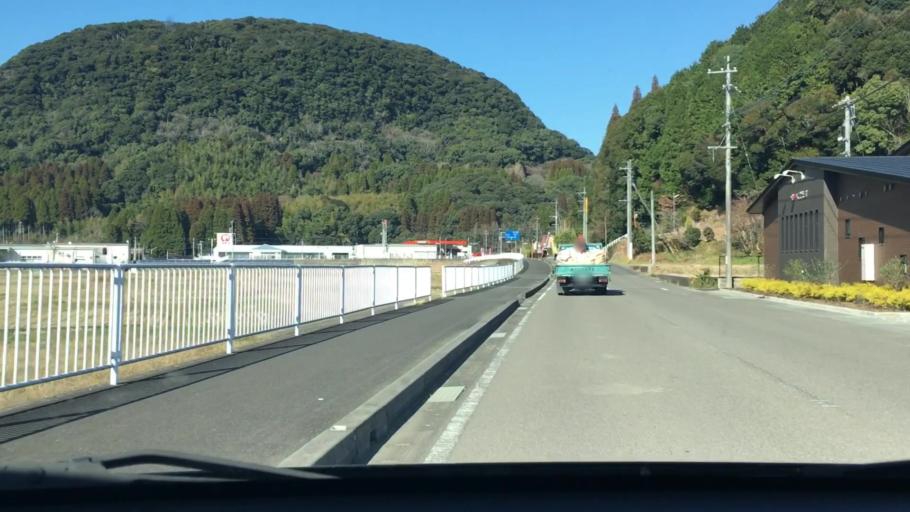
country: JP
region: Kagoshima
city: Satsumasendai
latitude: 31.7950
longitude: 130.4103
